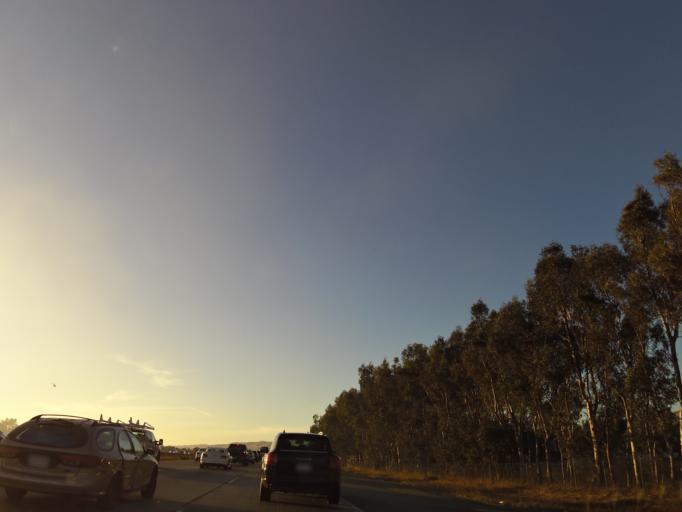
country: US
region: California
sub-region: Santa Clara County
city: San Martin
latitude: 37.0936
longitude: -121.6018
